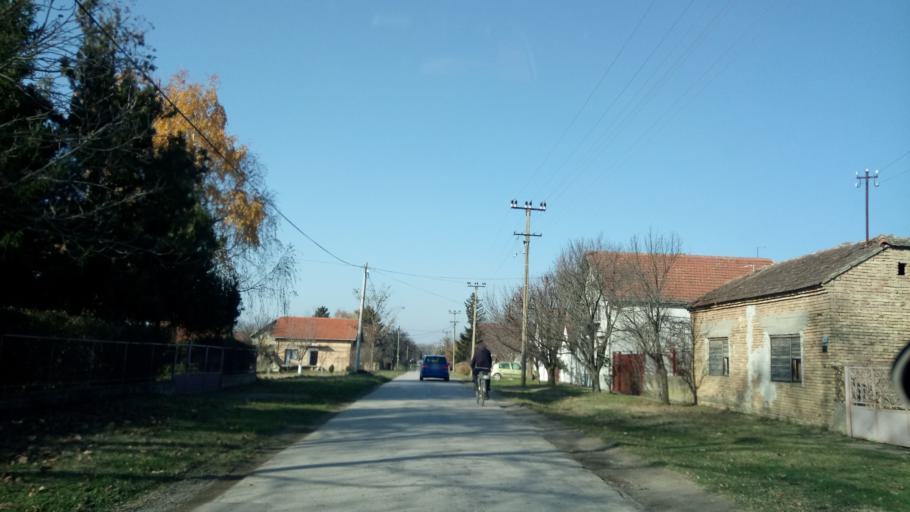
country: RS
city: Ljukovo
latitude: 45.0491
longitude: 20.0295
